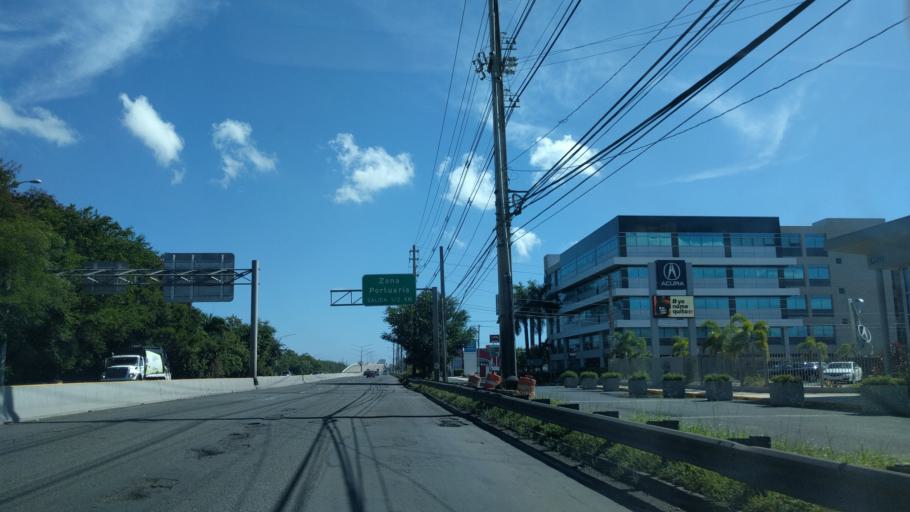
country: PR
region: Catano
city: Catano
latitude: 18.4241
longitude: -66.0964
